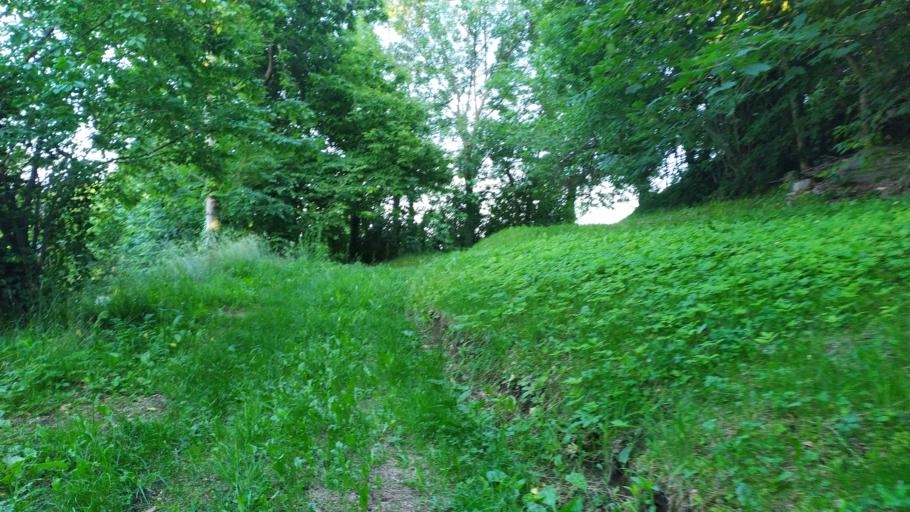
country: IT
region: Veneto
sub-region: Provincia di Vicenza
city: Torrebelvicino
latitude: 45.6836
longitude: 11.3328
